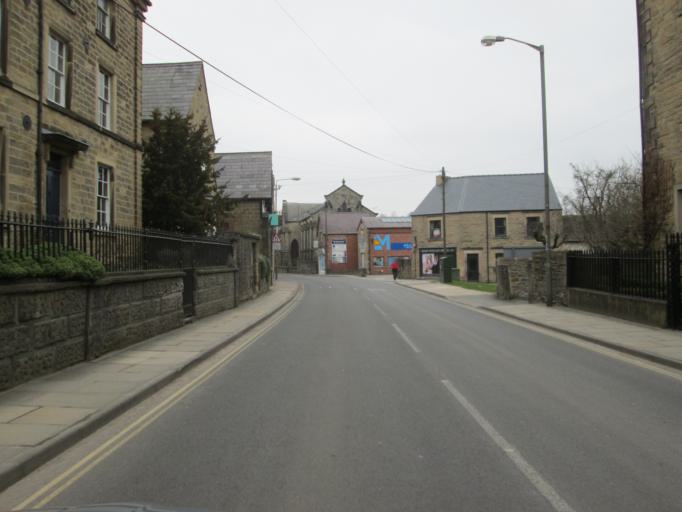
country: GB
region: England
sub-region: Derbyshire
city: Bakewell
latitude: 53.2137
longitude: -1.6766
